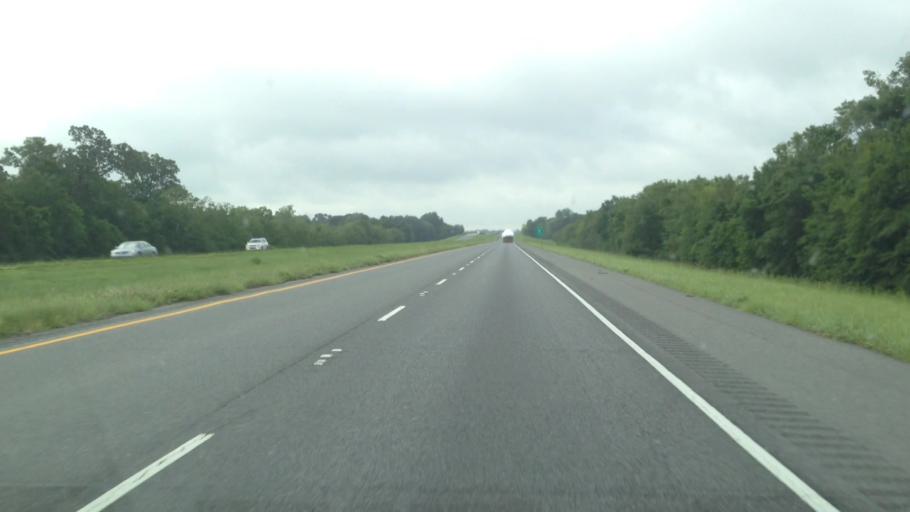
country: US
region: Louisiana
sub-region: Saint Landry Parish
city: Opelousas
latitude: 30.6599
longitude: -92.0653
